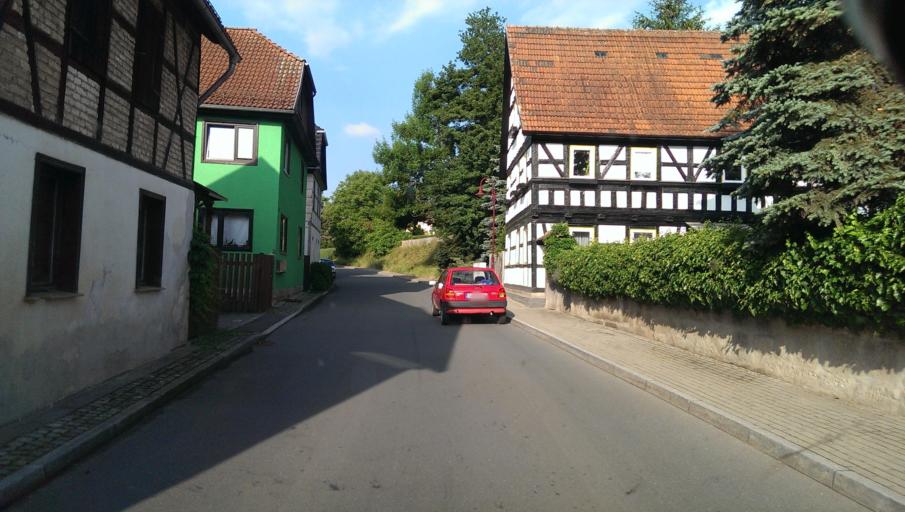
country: DE
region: Thuringia
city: Rottenbach
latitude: 50.6961
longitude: 11.2095
